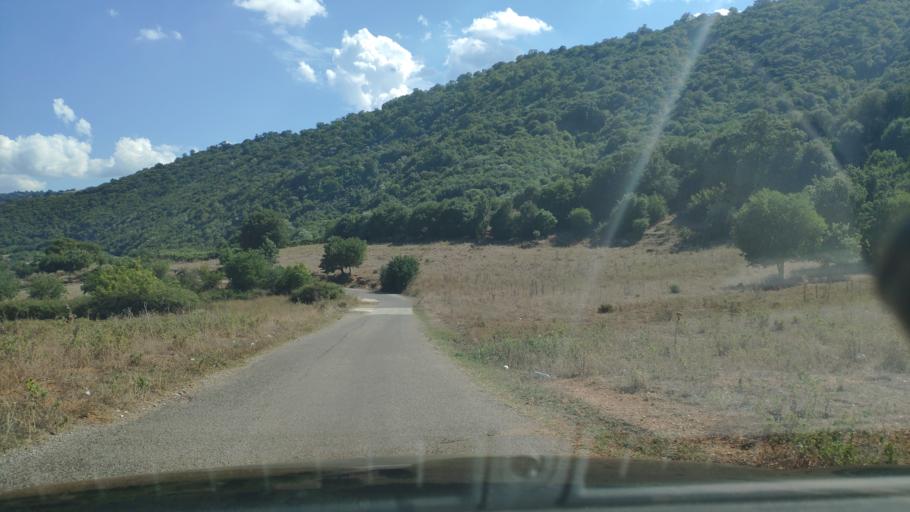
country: GR
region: West Greece
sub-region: Nomos Aitolias kai Akarnanias
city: Katouna
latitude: 38.8337
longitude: 21.0994
